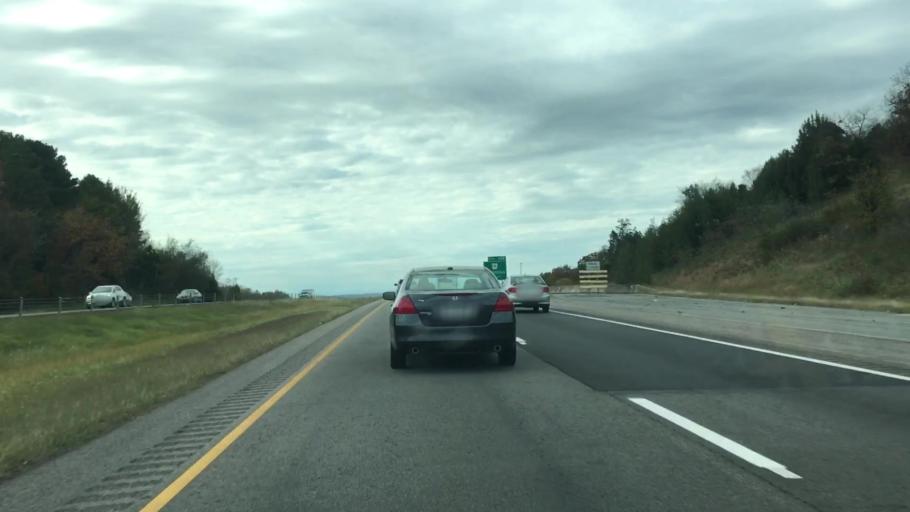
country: US
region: Arkansas
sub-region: Conway County
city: Morrilton
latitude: 35.1705
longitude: -92.6944
